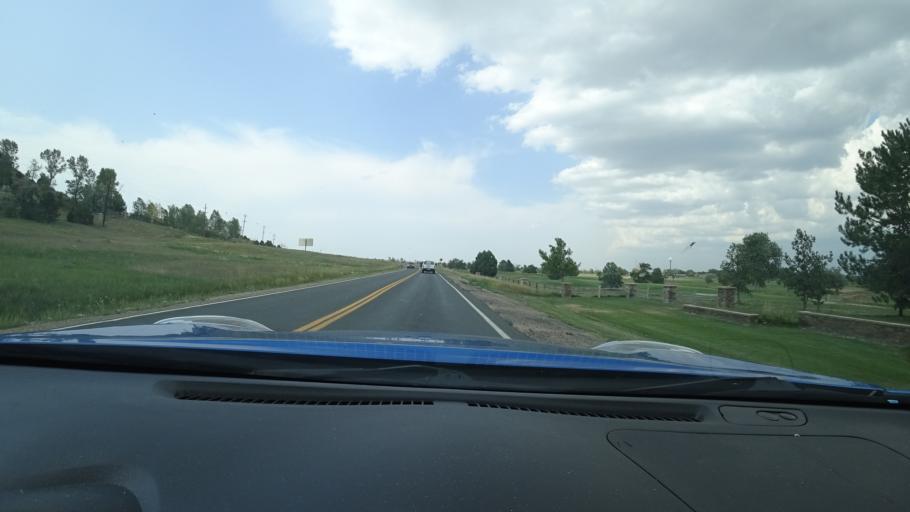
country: US
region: Colorado
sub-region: Adams County
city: Todd Creek
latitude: 39.9254
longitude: -104.8835
